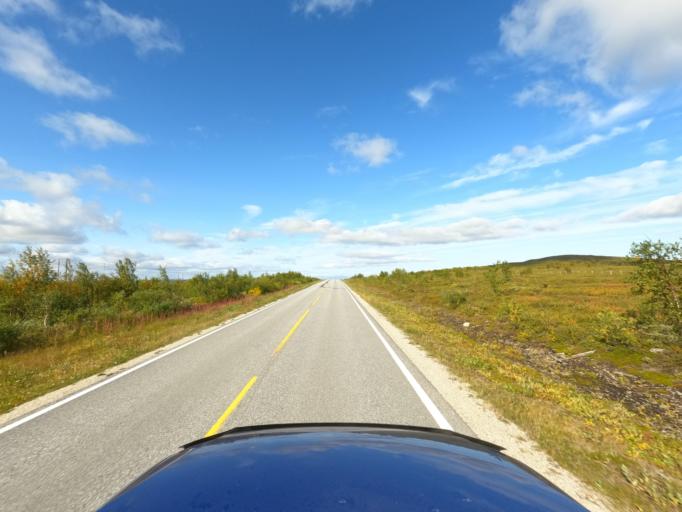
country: NO
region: Finnmark Fylke
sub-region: Karasjok
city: Karasjohka
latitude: 69.5565
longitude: 25.3993
